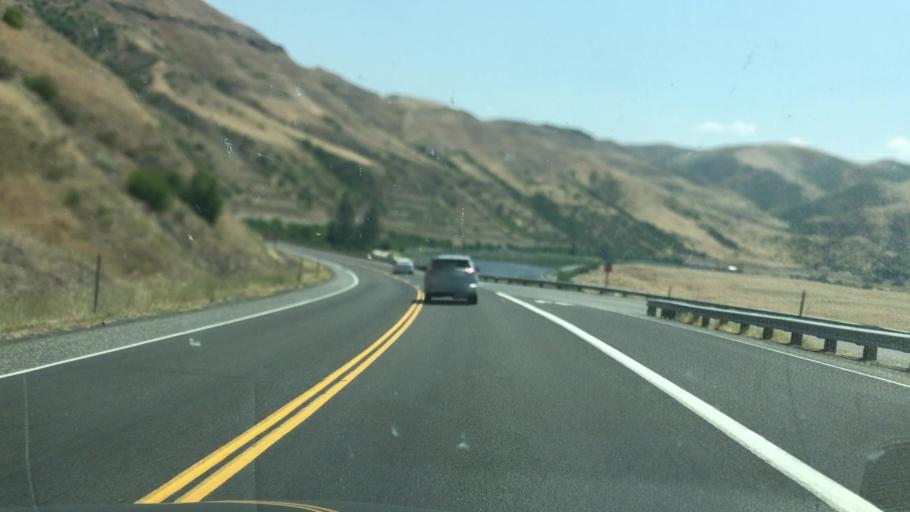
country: US
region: Idaho
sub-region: Idaho County
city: Grangeville
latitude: 45.7369
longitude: -116.3104
